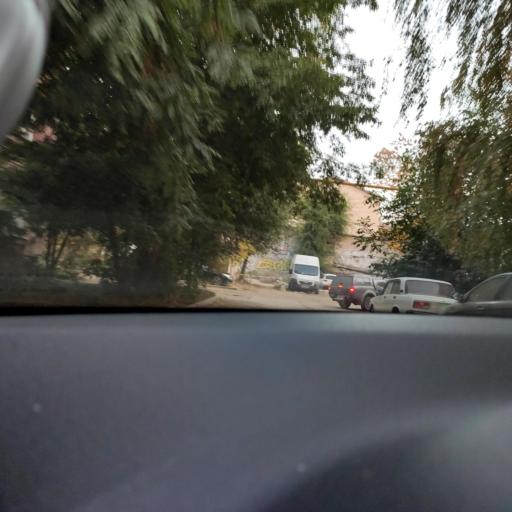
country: RU
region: Samara
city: Samara
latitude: 53.2117
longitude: 50.2468
